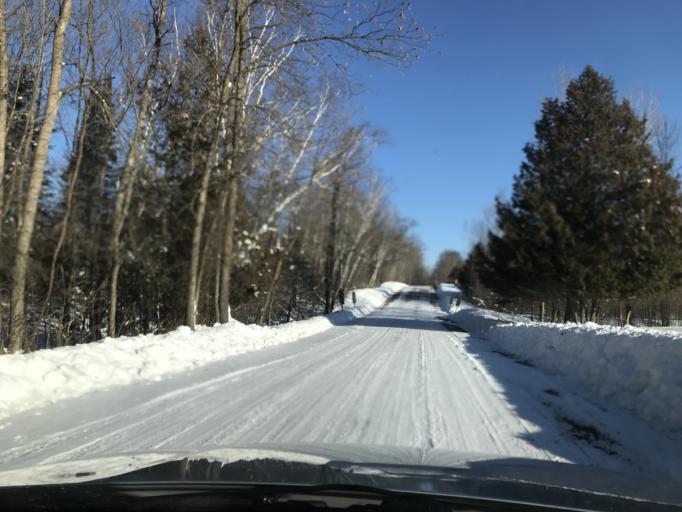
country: US
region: Wisconsin
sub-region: Oconto County
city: Oconto
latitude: 44.9534
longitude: -87.9770
